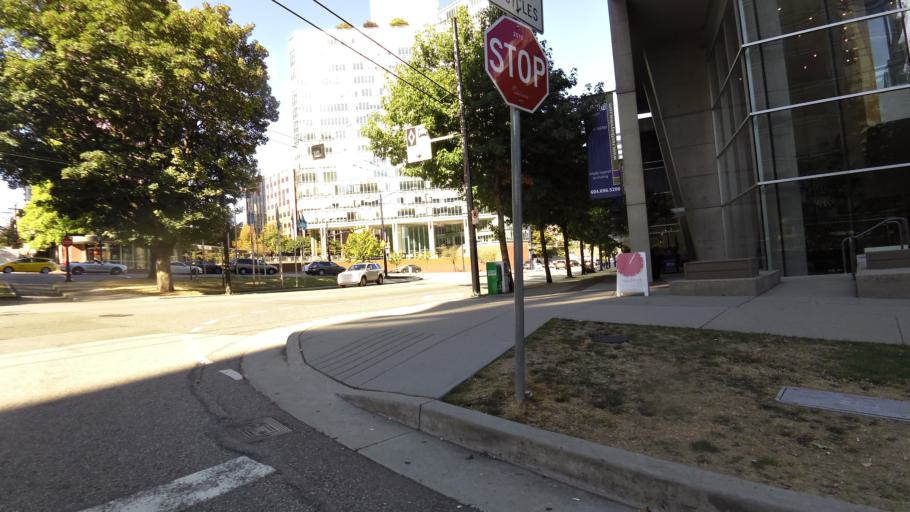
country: CA
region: British Columbia
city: West End
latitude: 49.2903
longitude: -123.1290
